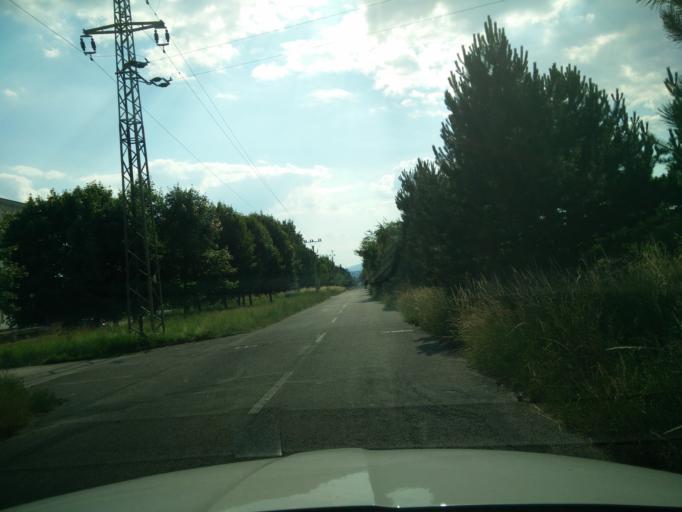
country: SK
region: Nitriansky
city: Prievidza
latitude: 48.7679
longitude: 18.6379
